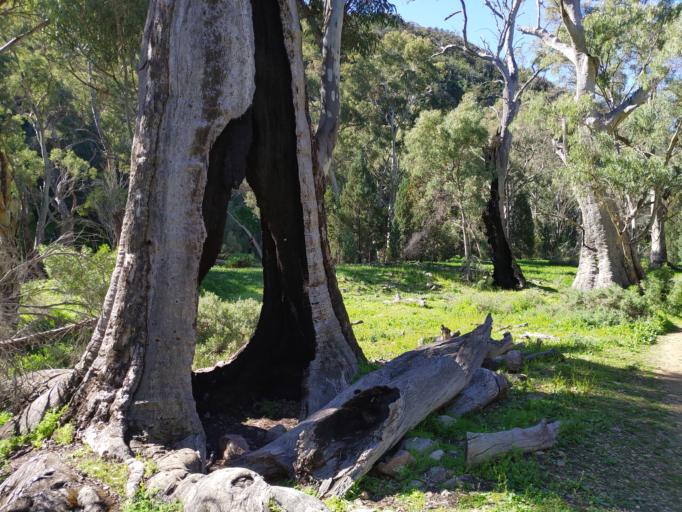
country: AU
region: South Australia
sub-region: Port Pirie City and Dists
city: Port Pirie
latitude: -32.8346
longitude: 138.0477
